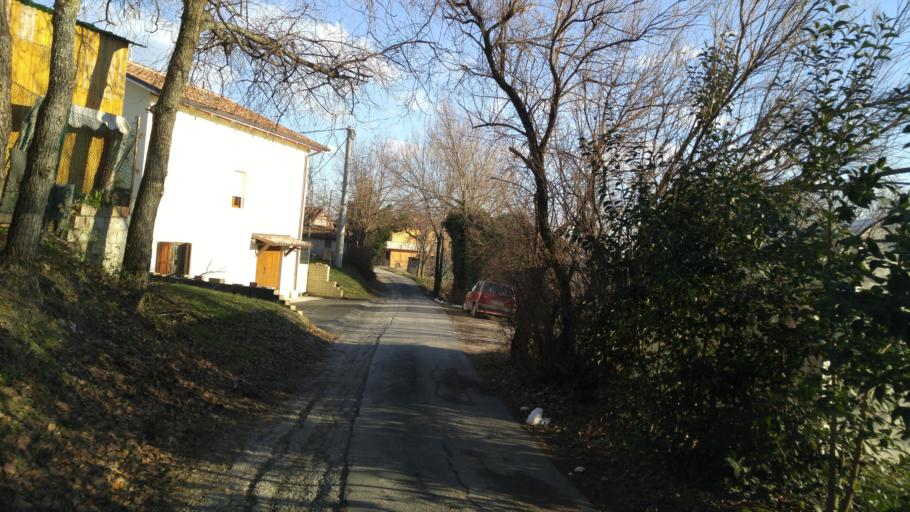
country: IT
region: The Marches
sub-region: Provincia di Pesaro e Urbino
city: Piagge
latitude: 43.7280
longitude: 12.9667
